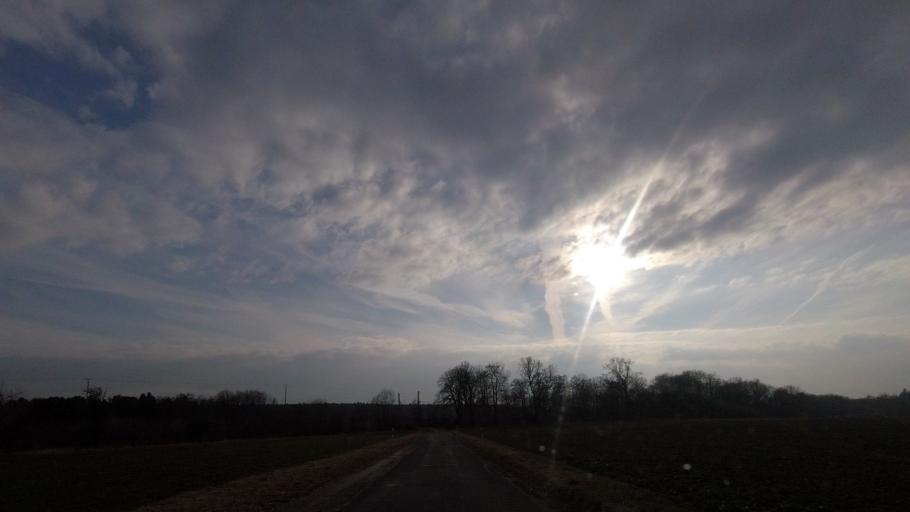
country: DE
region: Brandenburg
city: Belzig
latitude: 52.1646
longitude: 12.6788
